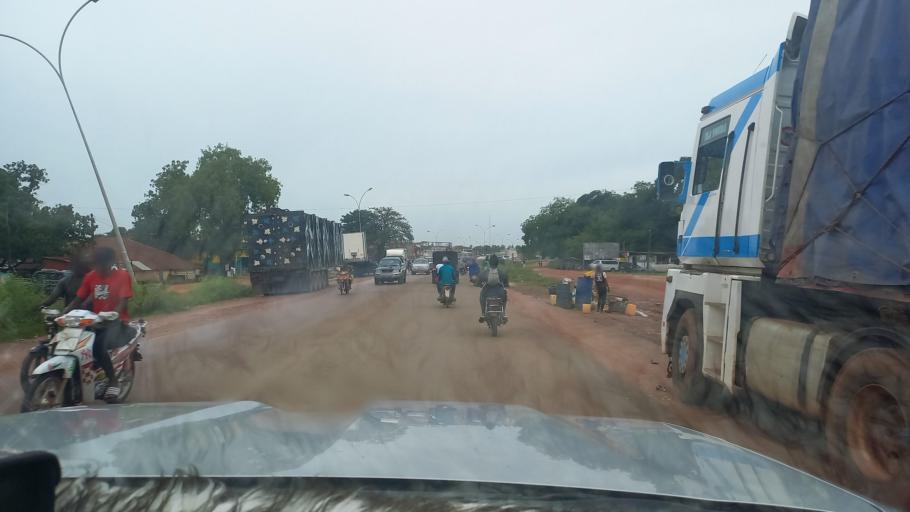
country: SN
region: Ziguinchor
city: Ziguinchor
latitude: 12.5683
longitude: -16.2700
